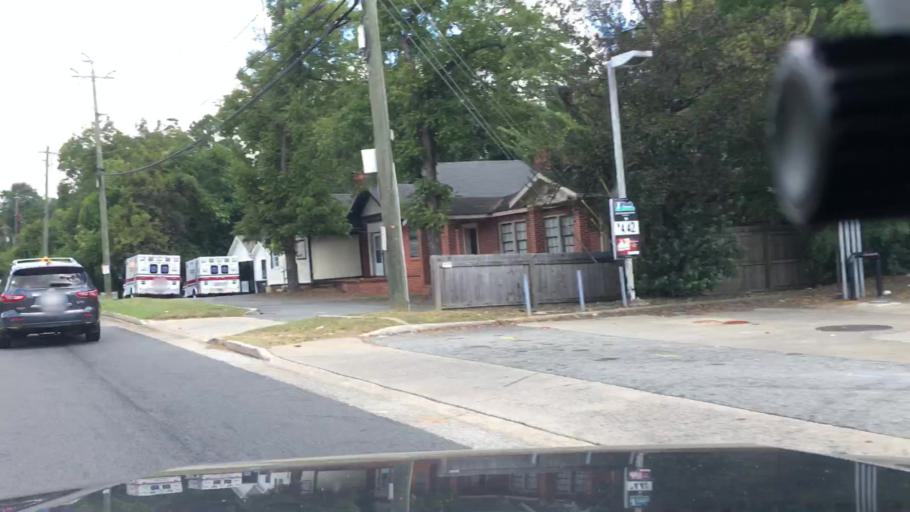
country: US
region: Georgia
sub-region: Bibb County
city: Macon
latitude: 32.8630
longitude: -83.6890
